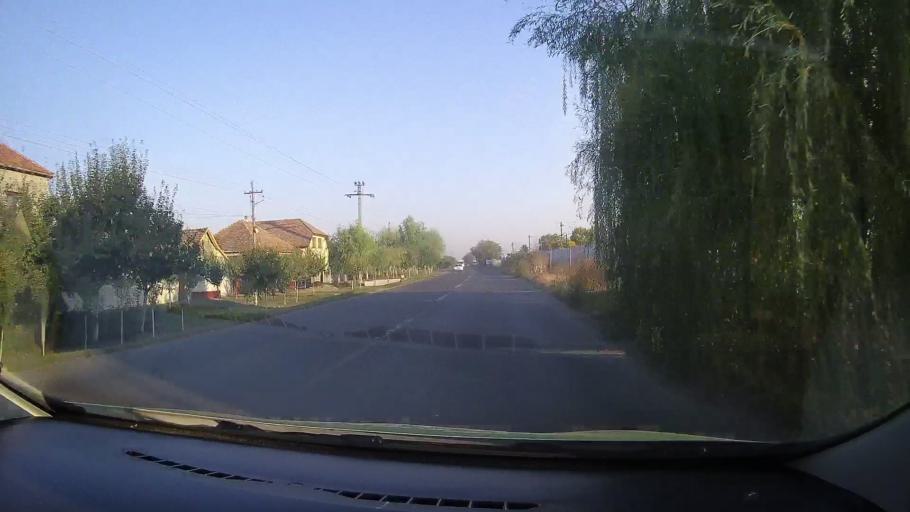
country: RO
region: Arad
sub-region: Comuna Sofronea
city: Sofronea
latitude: 46.2823
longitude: 21.3134
